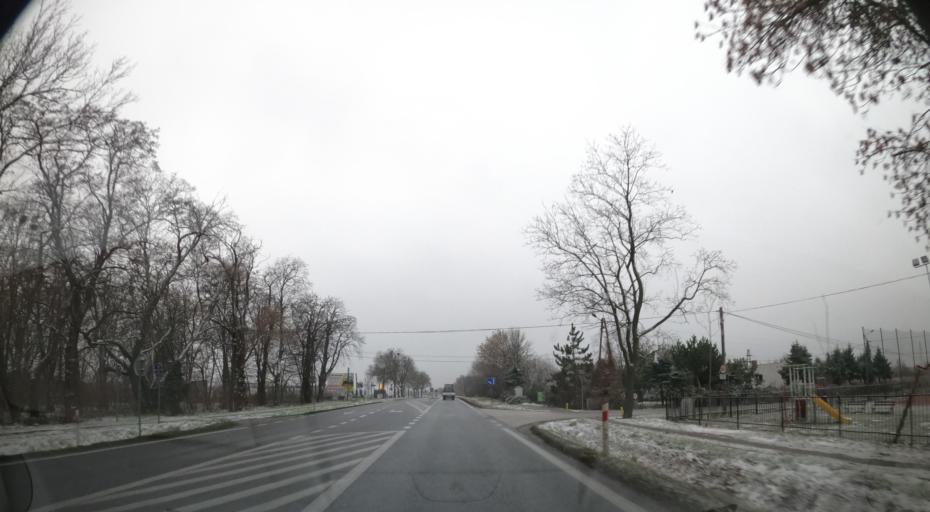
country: PL
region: Masovian Voivodeship
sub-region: Powiat warszawski zachodni
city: Kampinos
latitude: 52.2059
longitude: 20.4956
